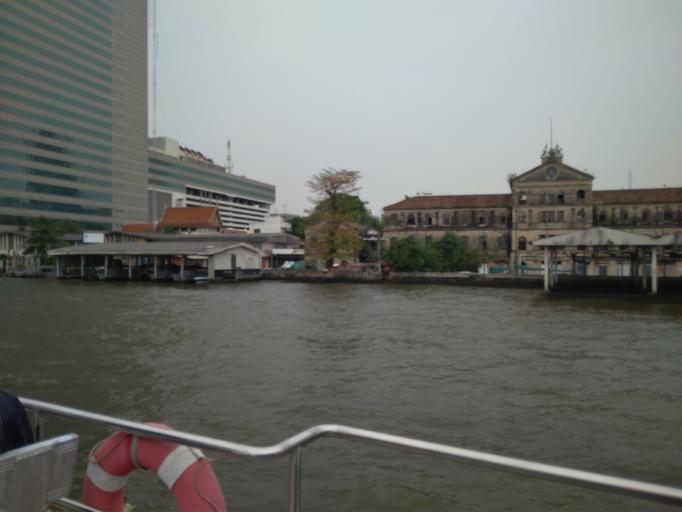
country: TH
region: Bangkok
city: Samphanthawong
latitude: 13.7251
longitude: 100.5130
